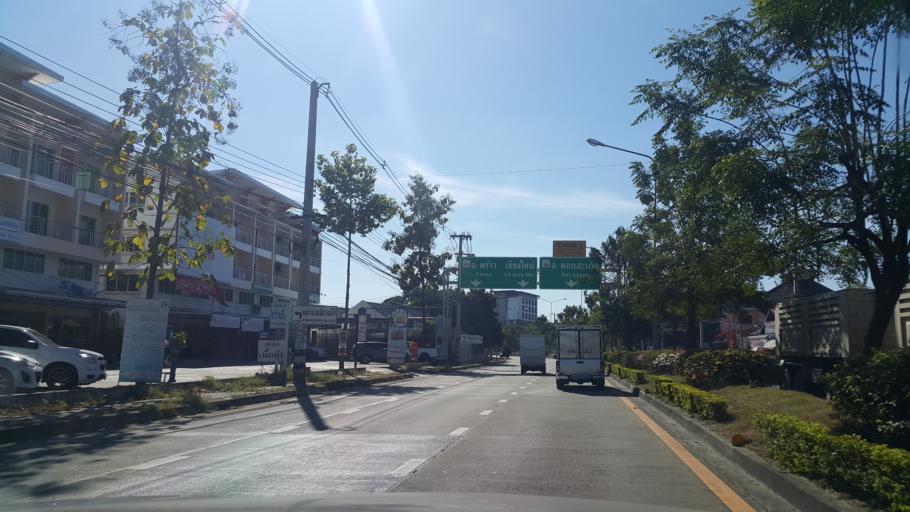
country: TH
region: Chiang Mai
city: Chiang Mai
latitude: 18.8262
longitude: 99.0072
